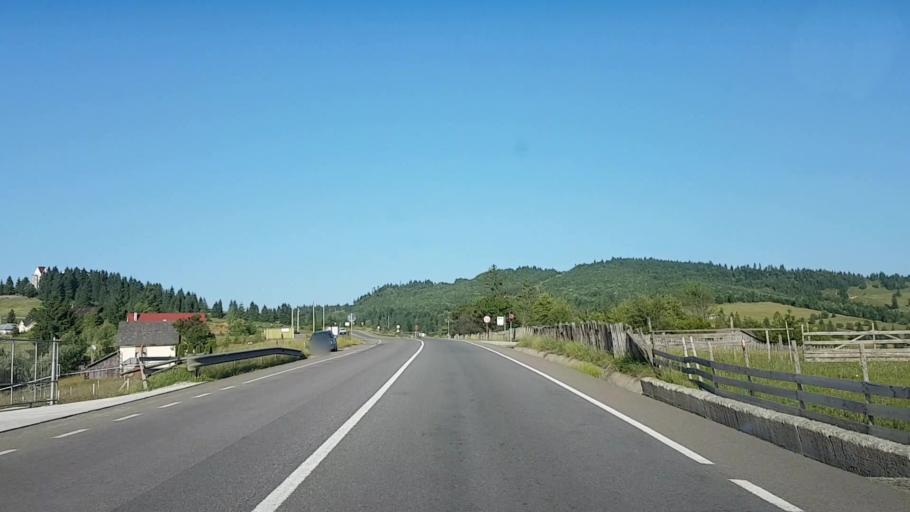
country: RO
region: Bistrita-Nasaud
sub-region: Comuna Lunca Ilvei
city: Lunca Ilvei
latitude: 47.2329
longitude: 24.9933
